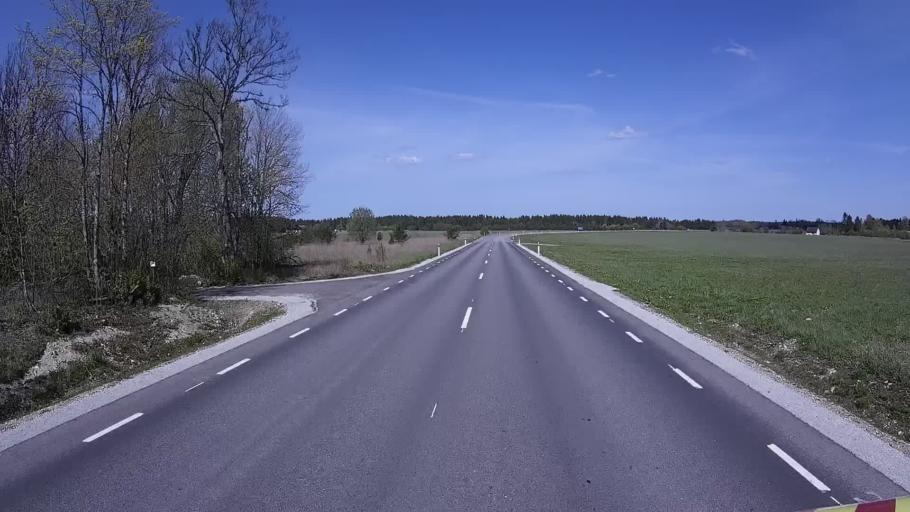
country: EE
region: Harju
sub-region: Paldiski linn
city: Paldiski
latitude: 59.2108
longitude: 24.0946
